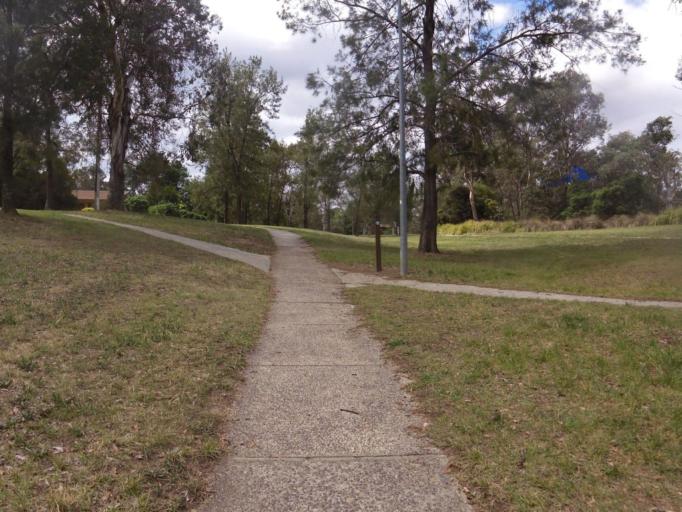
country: AU
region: Australian Capital Territory
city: Macarthur
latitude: -35.4086
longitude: 149.1278
